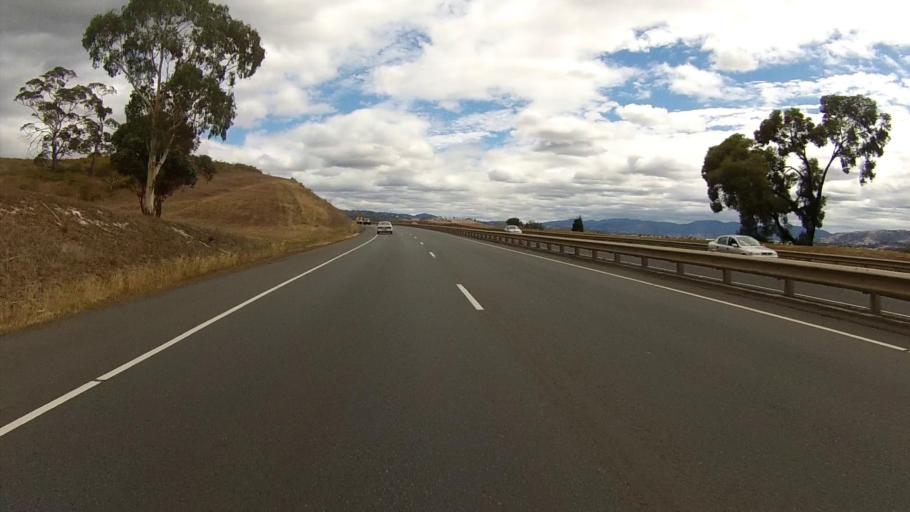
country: AU
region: Tasmania
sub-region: Glenorchy
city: Granton
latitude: -42.7642
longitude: 147.2350
